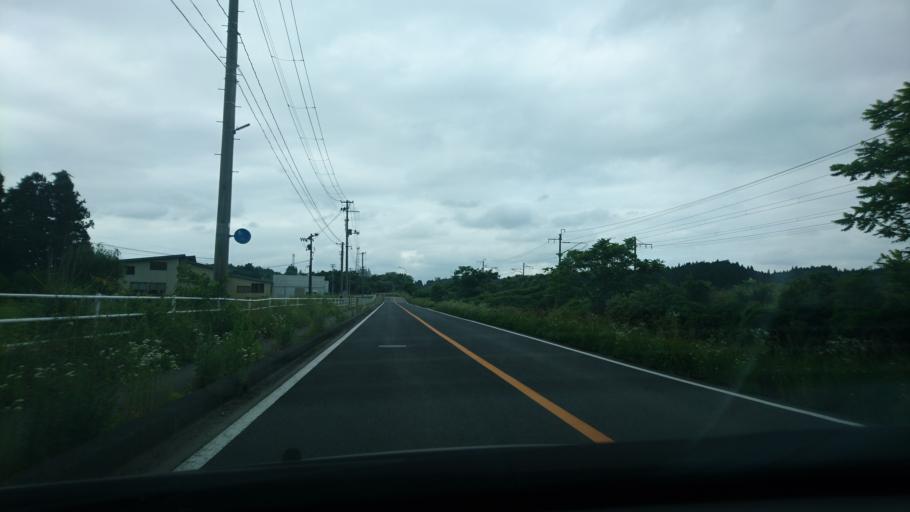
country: JP
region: Iwate
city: Ichinoseki
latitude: 38.8149
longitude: 141.1810
